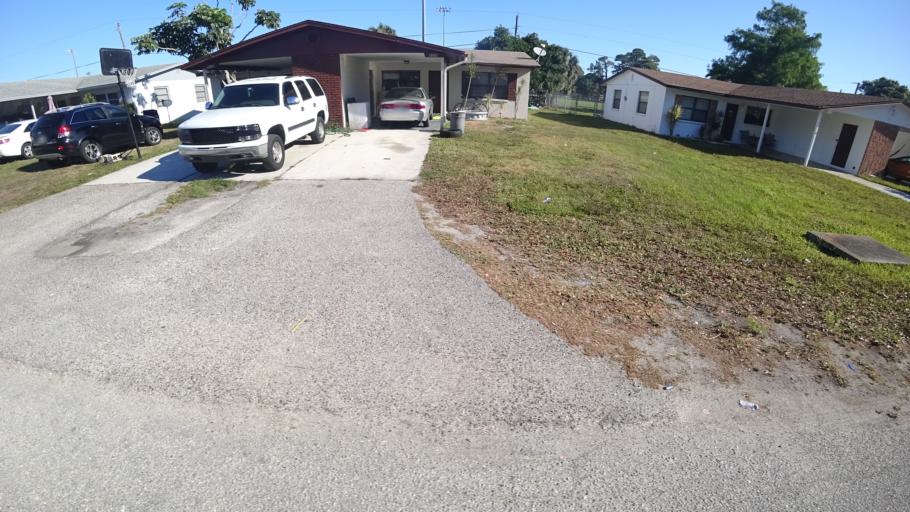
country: US
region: Florida
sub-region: Manatee County
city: Cortez
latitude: 27.4642
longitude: -82.6414
